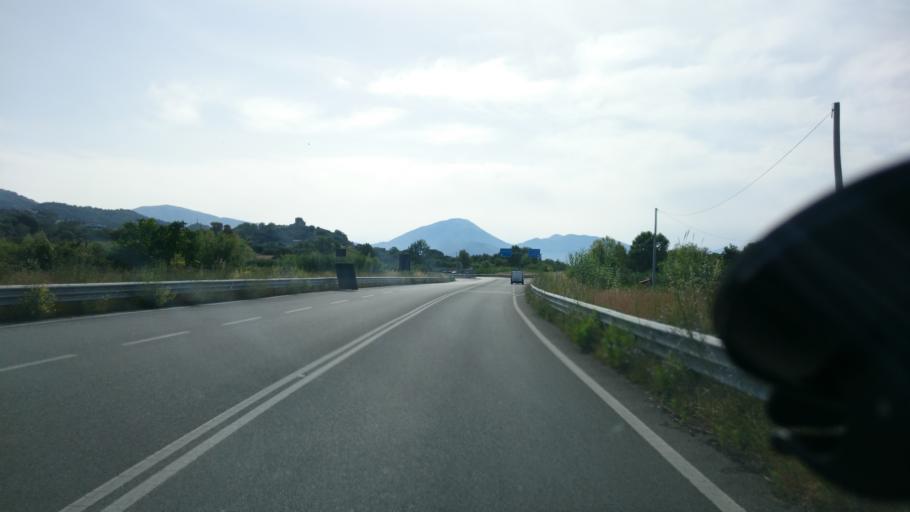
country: IT
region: Campania
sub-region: Provincia di Salerno
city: Policastro Bussentino
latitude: 40.0776
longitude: 15.5053
